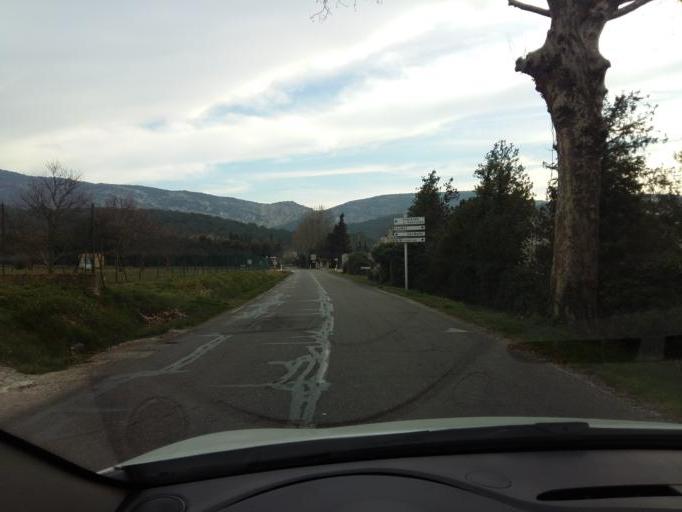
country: FR
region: Provence-Alpes-Cote d'Azur
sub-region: Departement du Vaucluse
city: Lagnes
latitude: 43.9169
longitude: 5.1040
